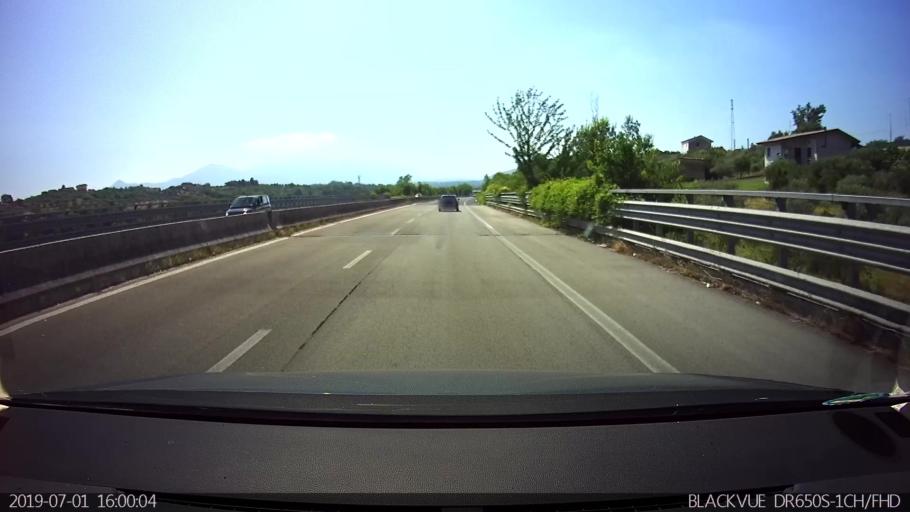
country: IT
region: Latium
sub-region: Provincia di Frosinone
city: San Giuseppe le Prata-Cotropagno
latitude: 41.6616
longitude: 13.4060
